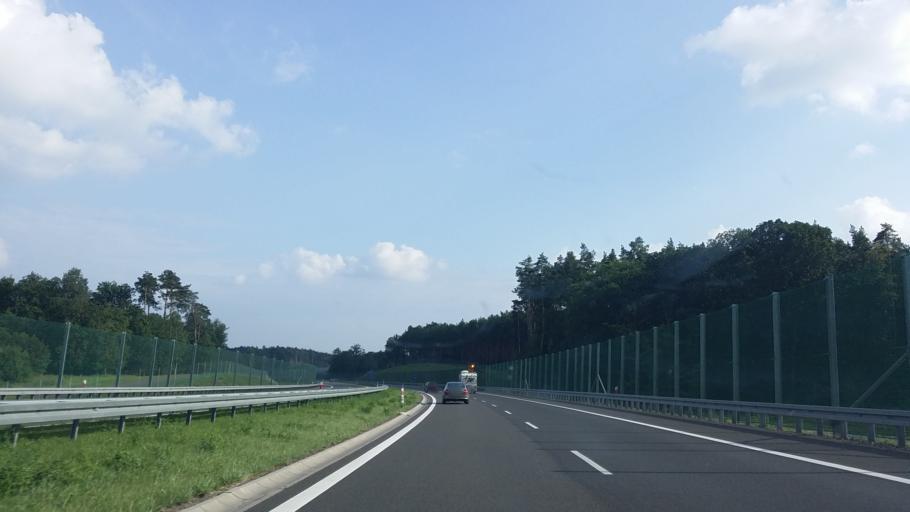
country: PL
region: Lubusz
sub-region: Powiat miedzyrzecki
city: Miedzyrzecz
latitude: 52.4887
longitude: 15.5499
